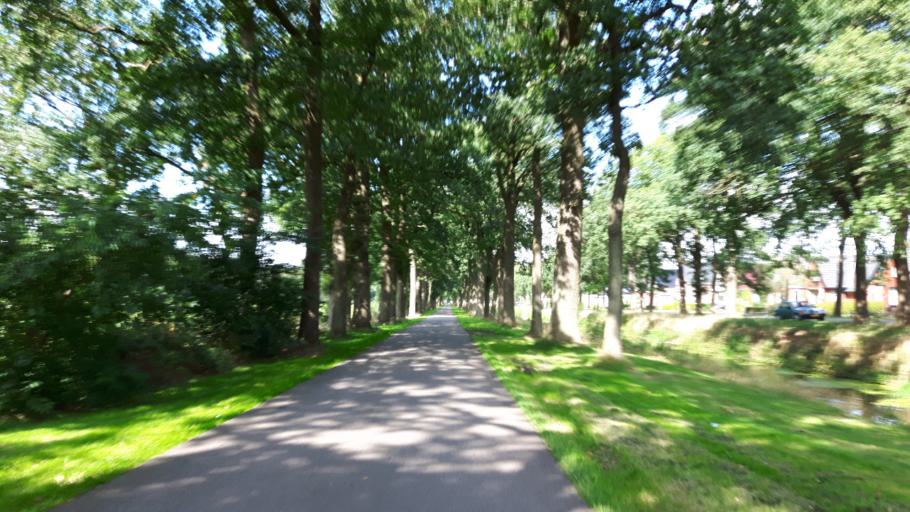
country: NL
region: Friesland
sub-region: Gemeente Smallingerland
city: Drachtstercompagnie
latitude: 53.0761
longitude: 6.2617
